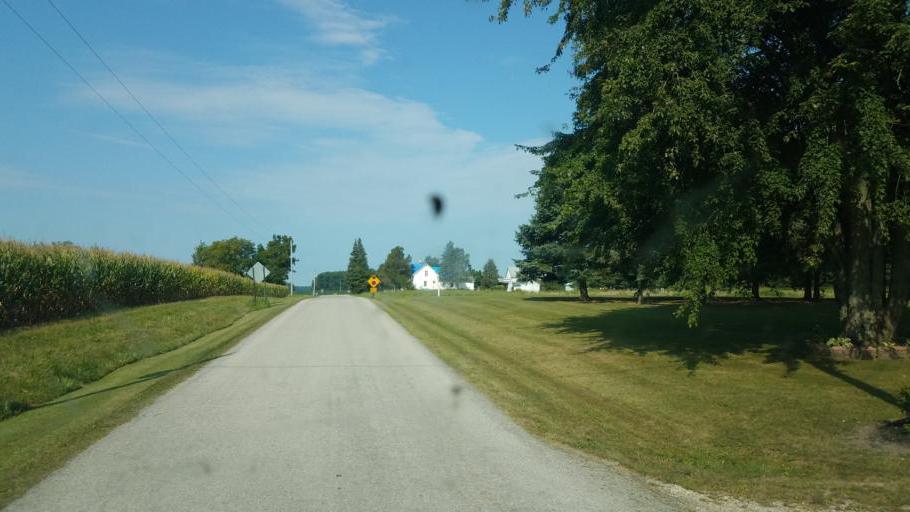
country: US
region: Ohio
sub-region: Morrow County
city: Cardington
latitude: 40.5030
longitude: -82.9458
